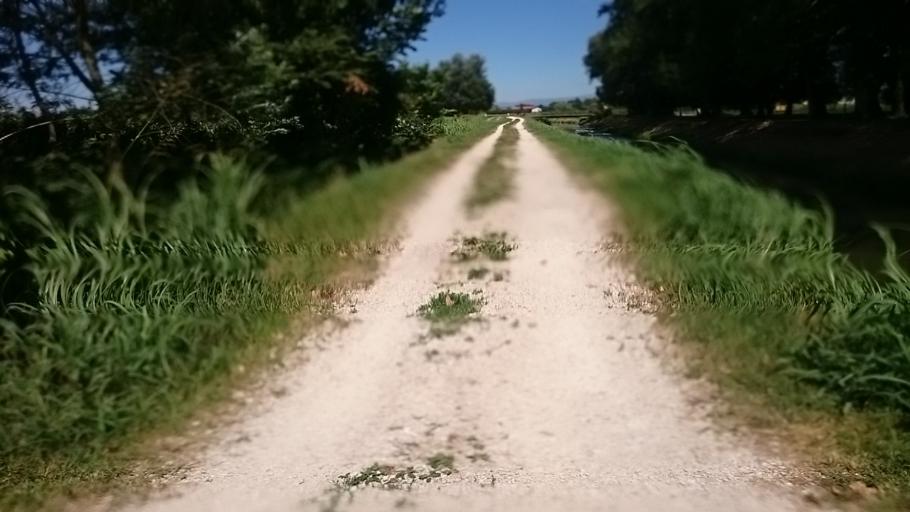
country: IT
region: Veneto
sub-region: Provincia di Padova
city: Codiverno
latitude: 45.4890
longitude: 11.9465
